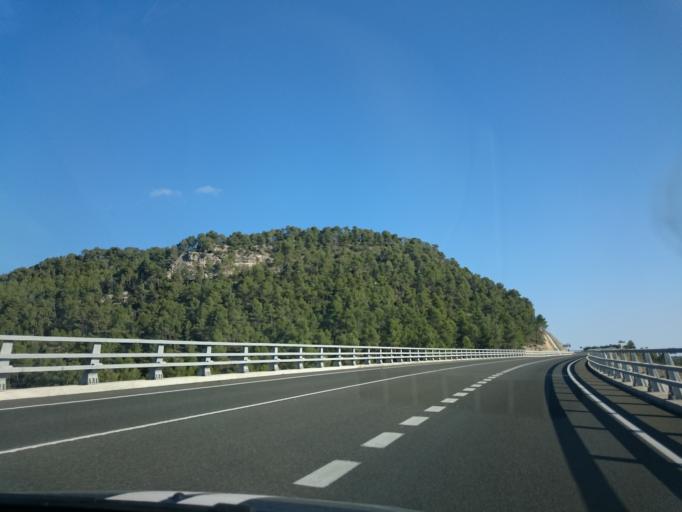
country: ES
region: Catalonia
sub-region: Provincia de Barcelona
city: Castelloli
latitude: 41.6082
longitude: 1.6776
